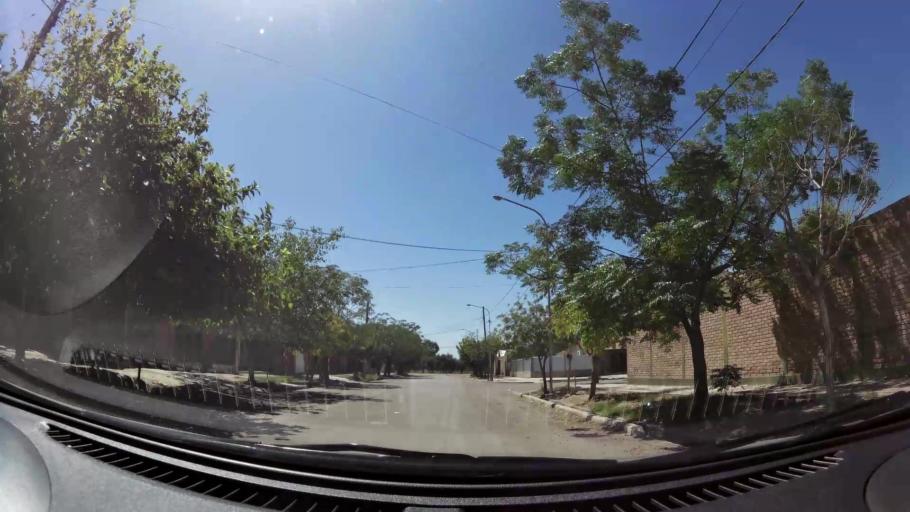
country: AR
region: Mendoza
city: Villa Nueva
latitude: -32.8787
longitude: -68.7932
